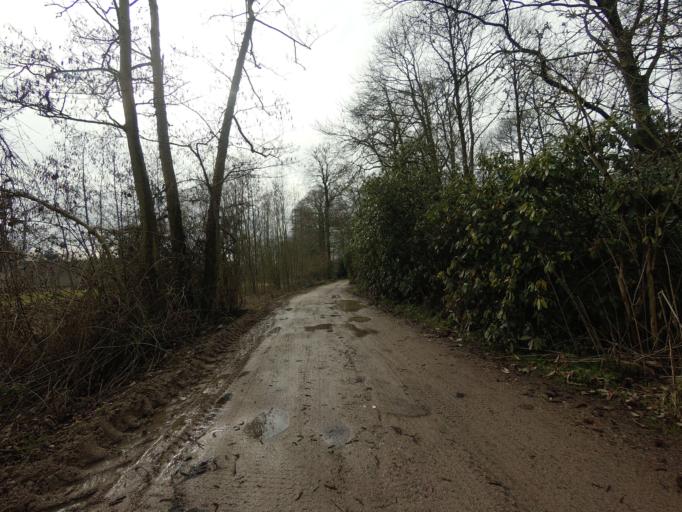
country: BE
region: Flanders
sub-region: Provincie Antwerpen
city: Aartselaar
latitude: 51.1400
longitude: 4.3634
